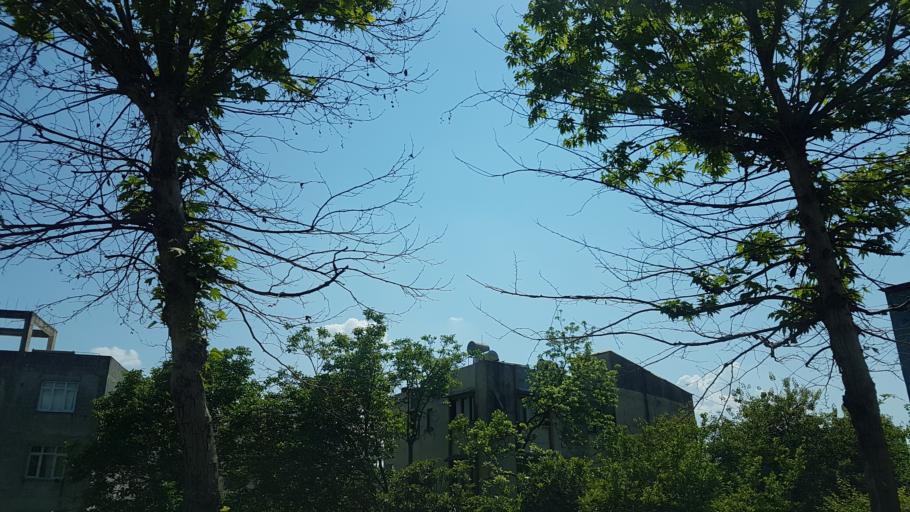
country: TR
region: Adana
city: Adana
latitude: 37.0234
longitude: 35.3689
